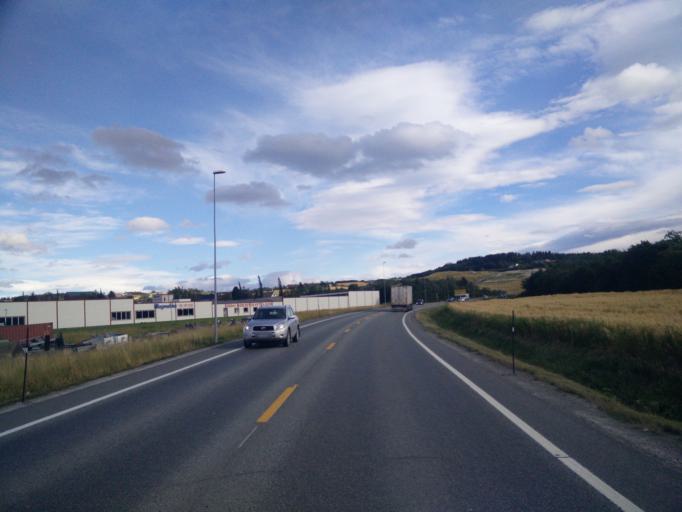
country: NO
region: Sor-Trondelag
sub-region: Melhus
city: Melhus
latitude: 63.3241
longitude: 10.3197
